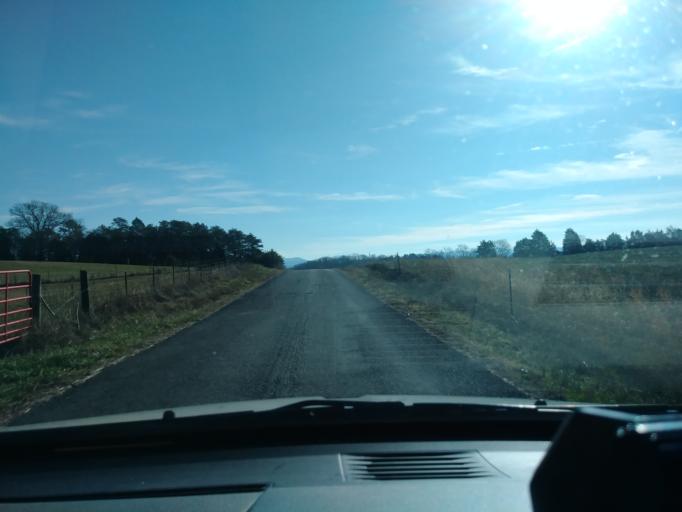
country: US
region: Tennessee
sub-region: Greene County
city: Greeneville
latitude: 36.0829
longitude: -82.8968
